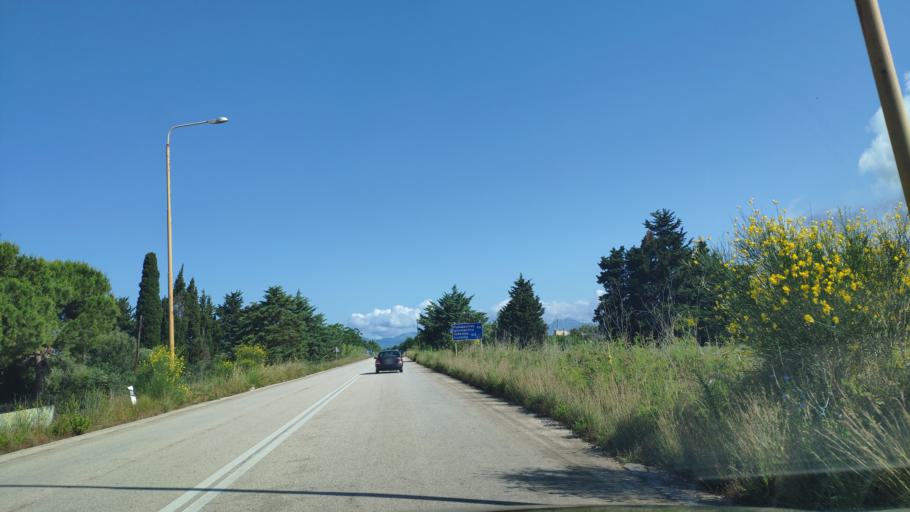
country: GR
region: Epirus
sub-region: Nomos Prevezis
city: Preveza
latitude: 38.9647
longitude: 20.7259
